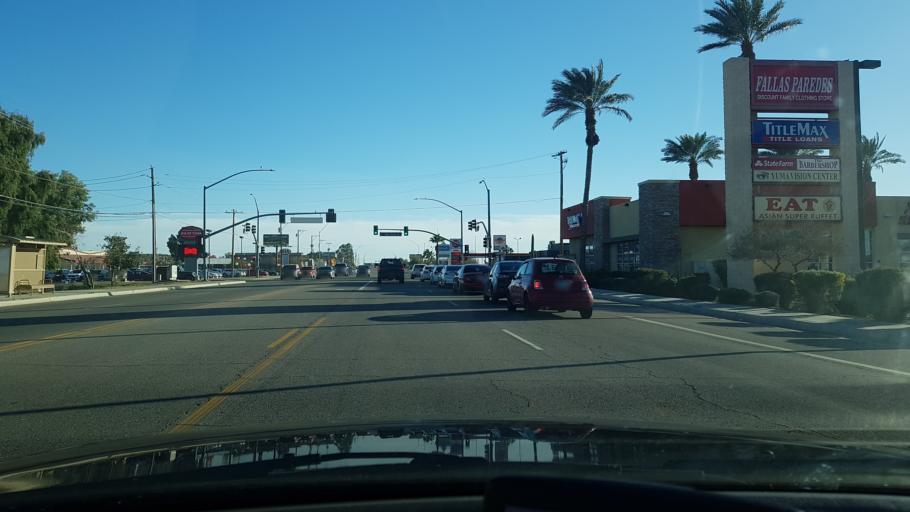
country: US
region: Arizona
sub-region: Yuma County
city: Yuma
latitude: 32.6776
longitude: -114.5989
